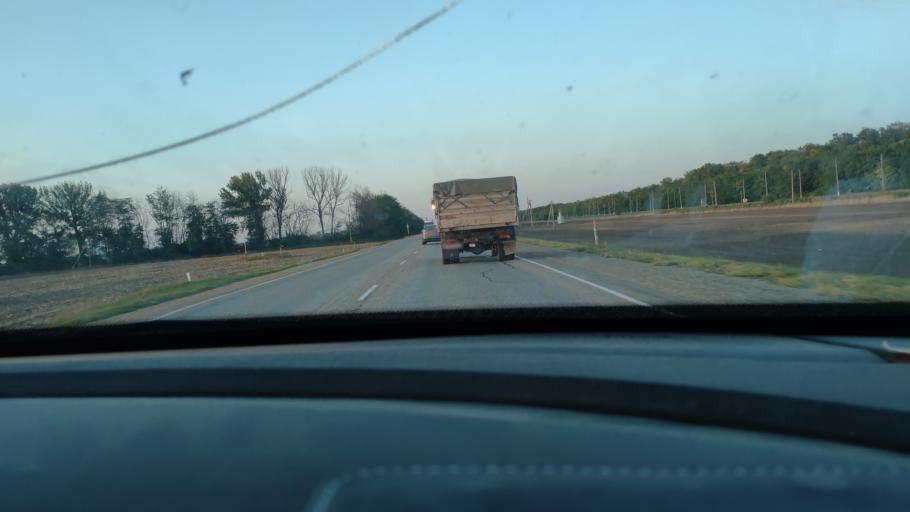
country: RU
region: Krasnodarskiy
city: Starominskaya
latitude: 46.4761
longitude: 39.0482
